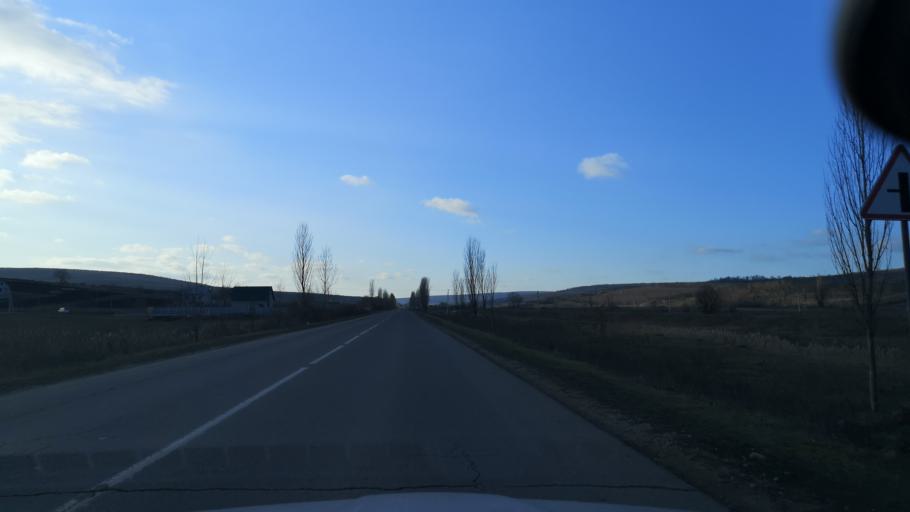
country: MD
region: Orhei
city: Orhei
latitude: 47.3436
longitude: 28.7555
